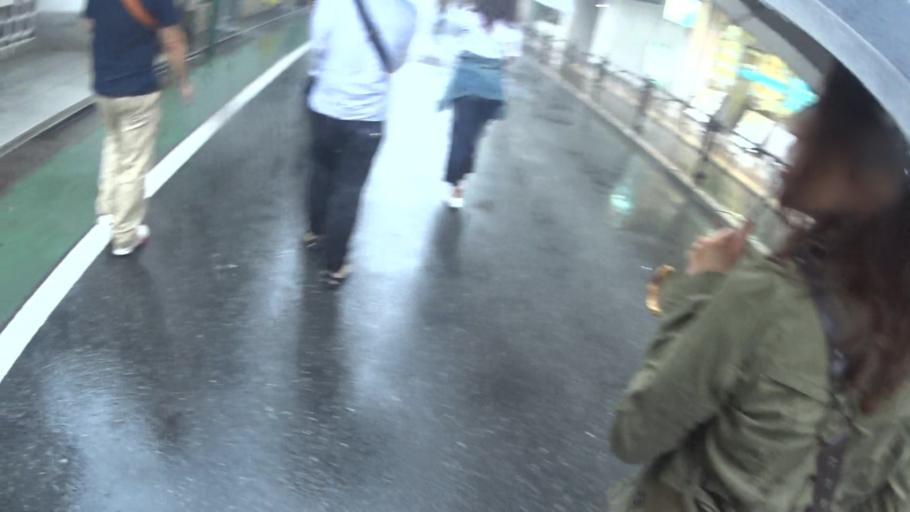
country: JP
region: Tokyo
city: Tokyo
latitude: 35.7376
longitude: 139.6698
